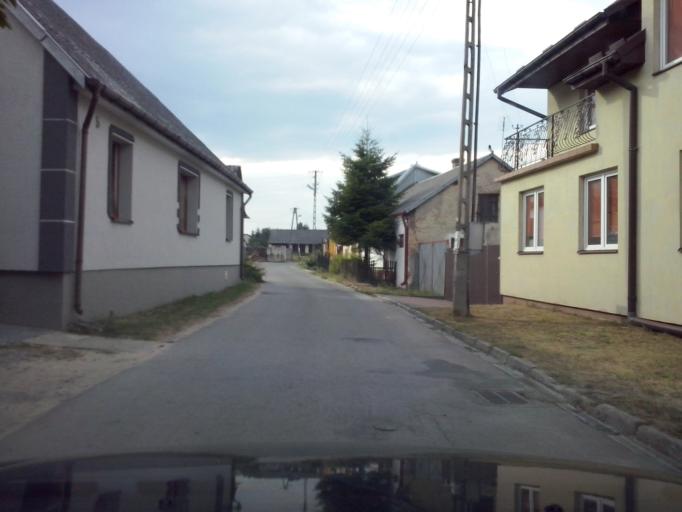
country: PL
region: Swietokrzyskie
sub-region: Powiat kielecki
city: Rakow
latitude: 50.6711
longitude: 21.0420
